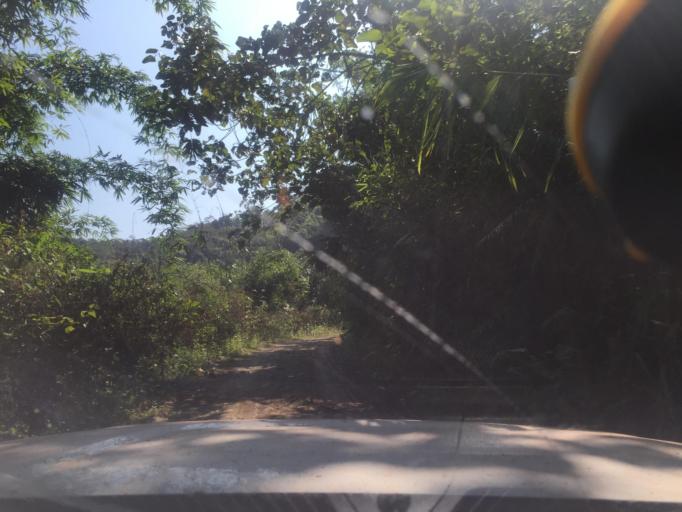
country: LA
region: Phongsali
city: Phongsali
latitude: 21.7053
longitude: 102.4006
